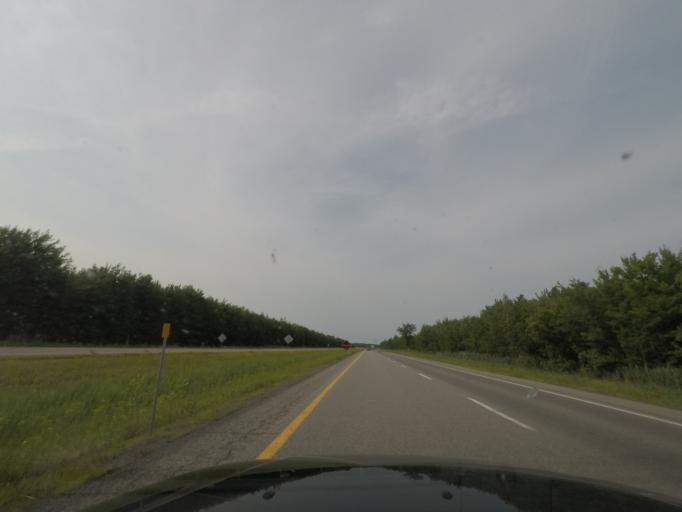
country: CA
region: Quebec
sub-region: Monteregie
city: Napierville
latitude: 45.1522
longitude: -73.4677
